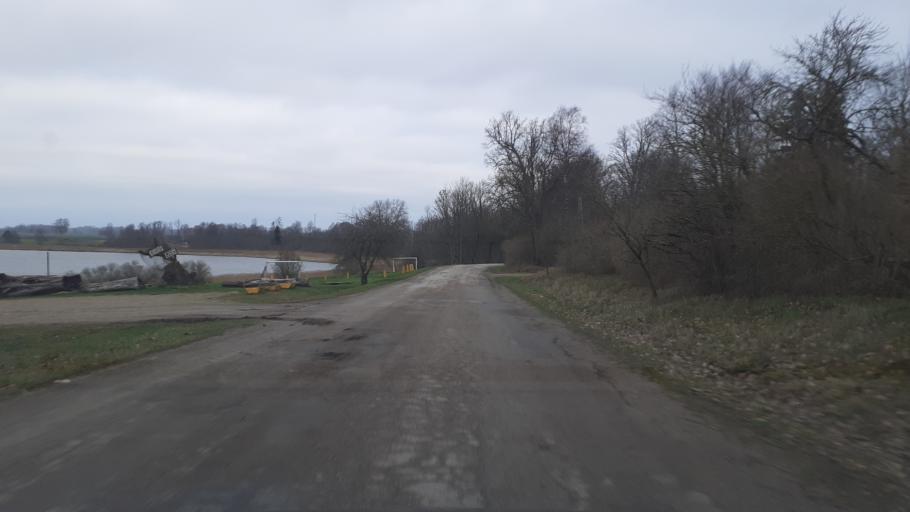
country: LV
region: Aizpute
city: Aizpute
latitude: 56.7998
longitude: 21.6658
